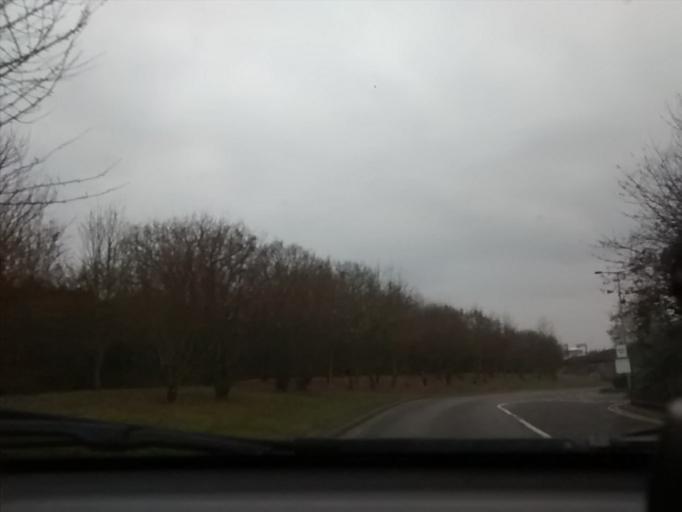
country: GB
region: England
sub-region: Essex
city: Stansted
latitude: 51.8703
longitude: 0.1944
